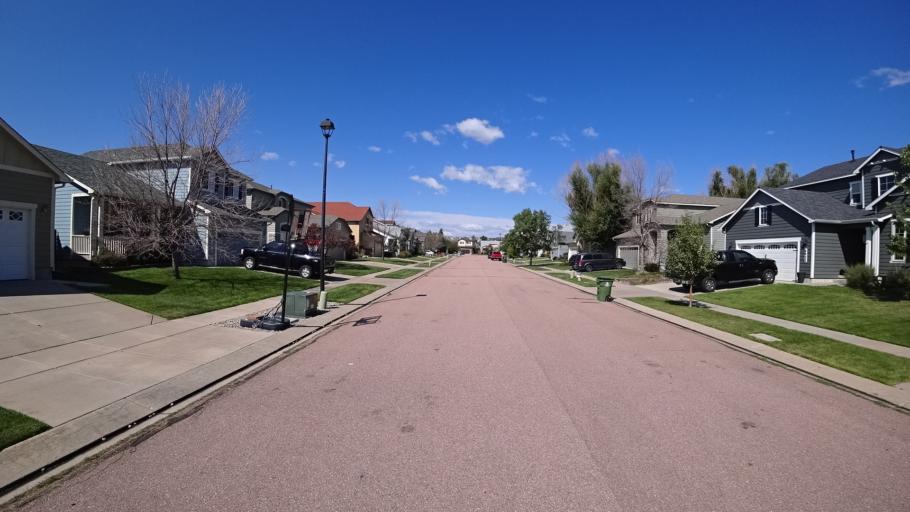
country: US
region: Colorado
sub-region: El Paso County
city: Cimarron Hills
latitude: 38.9230
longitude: -104.6976
